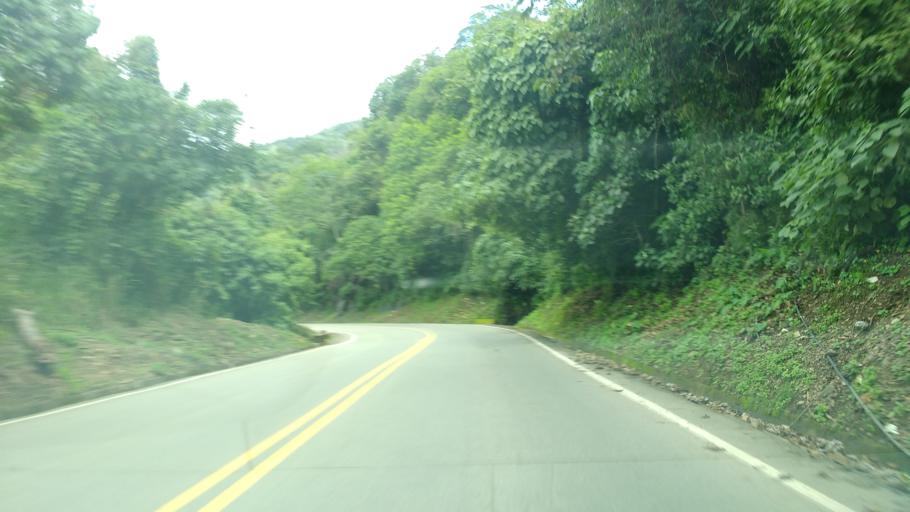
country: CO
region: Antioquia
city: Amaga
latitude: 6.0606
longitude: -75.7368
